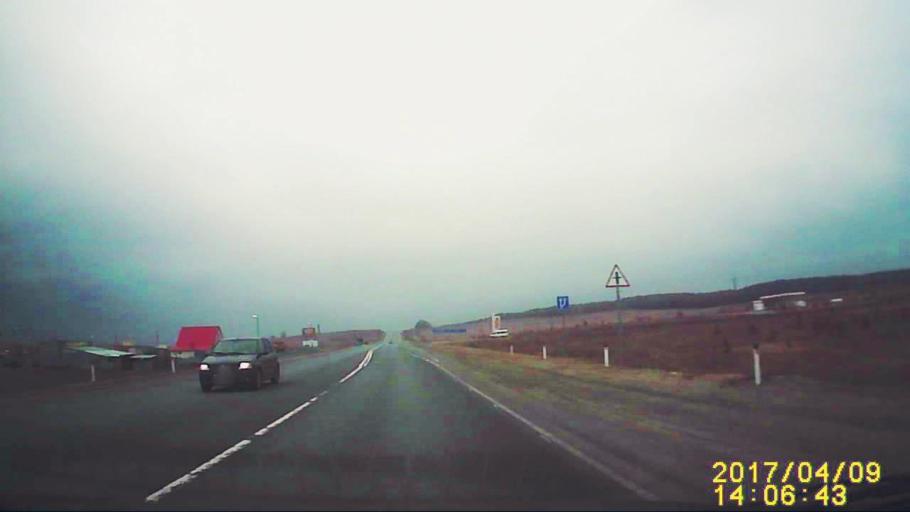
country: RU
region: Ulyanovsk
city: Silikatnyy
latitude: 54.0049
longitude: 48.2205
